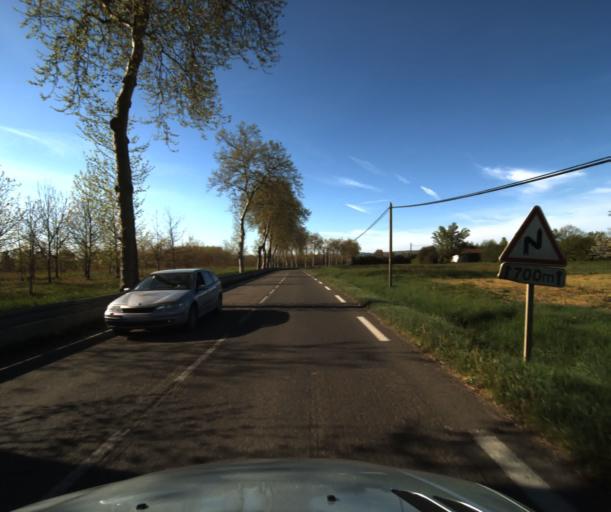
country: FR
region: Midi-Pyrenees
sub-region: Departement du Tarn-et-Garonne
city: Montbeton
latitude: 44.0577
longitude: 1.2909
